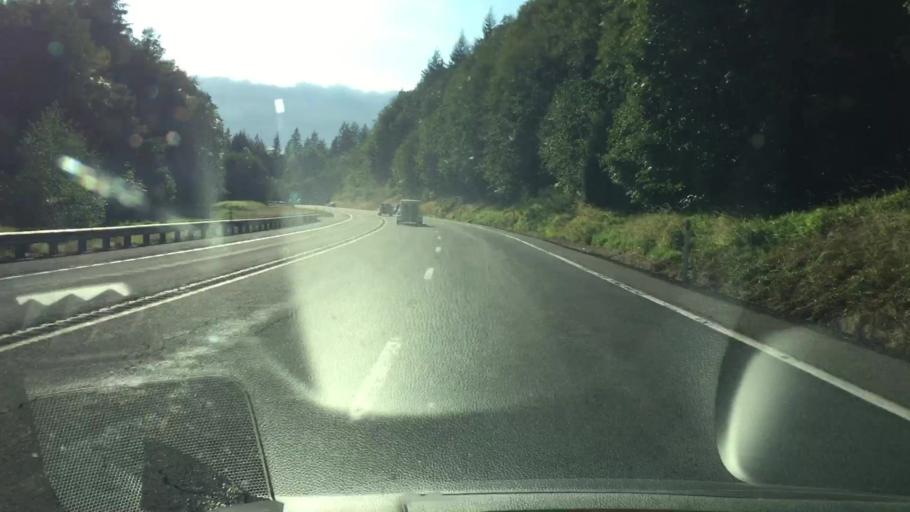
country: US
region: Washington
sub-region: Lewis County
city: Morton
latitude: 46.5462
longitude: -122.3412
